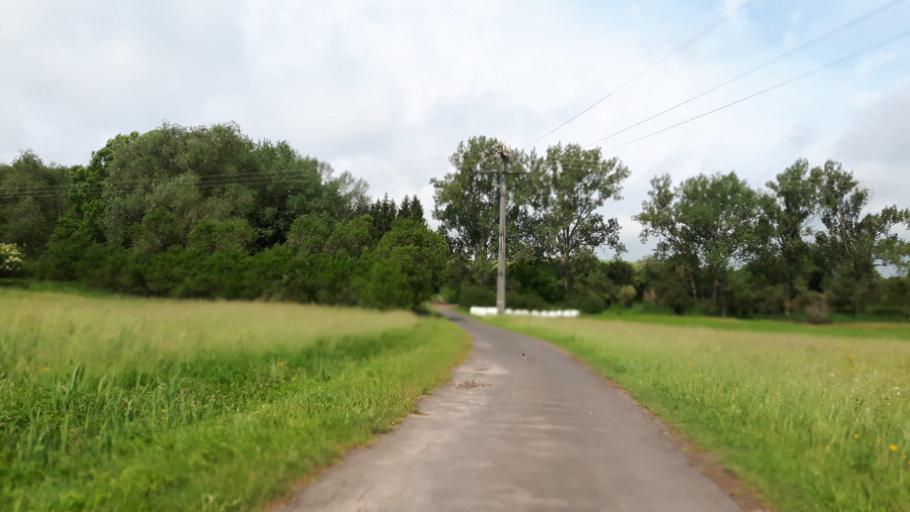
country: DE
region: Bavaria
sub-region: Regierungsbezirk Unterfranken
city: Sulzfeld
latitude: 50.2617
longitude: 10.3987
